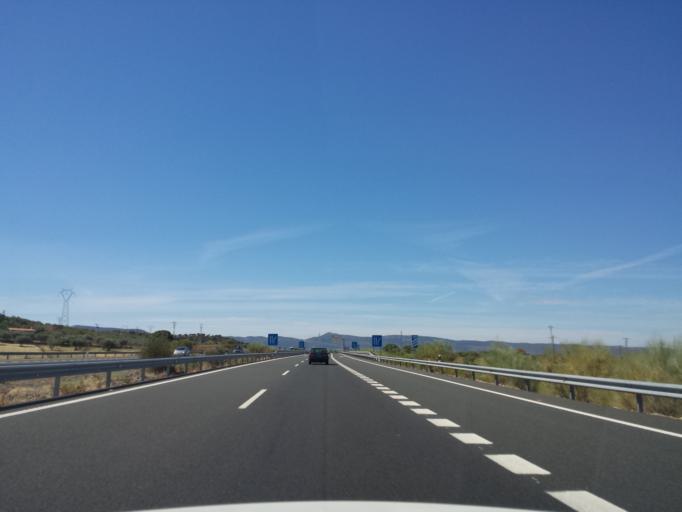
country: ES
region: Extremadura
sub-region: Provincia de Caceres
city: Almaraz
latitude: 39.8139
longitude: -5.6659
